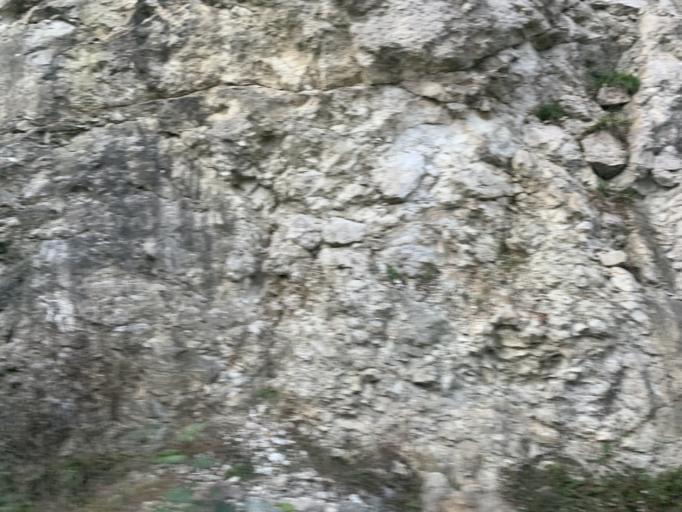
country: TR
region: Trabzon
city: Dernekpazari
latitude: 40.8225
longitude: 40.2663
